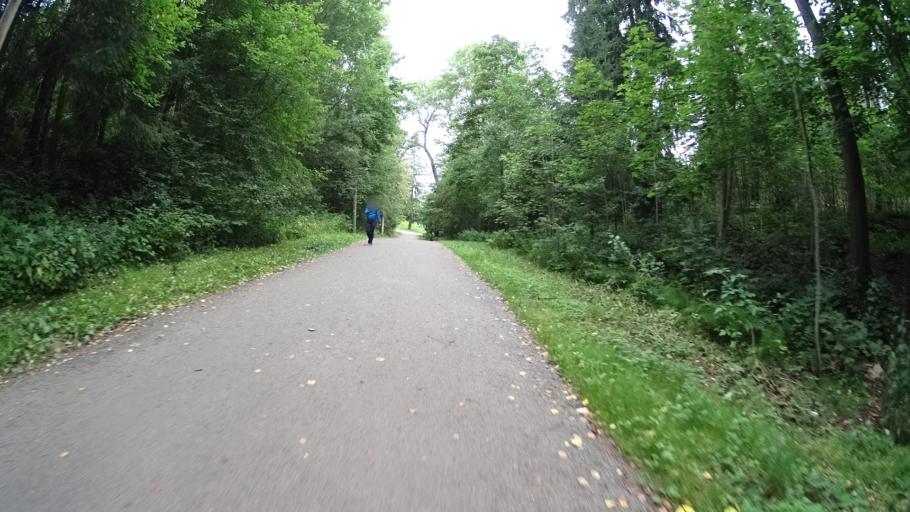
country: FI
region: Uusimaa
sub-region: Helsinki
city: Helsinki
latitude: 60.2298
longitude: 24.9817
